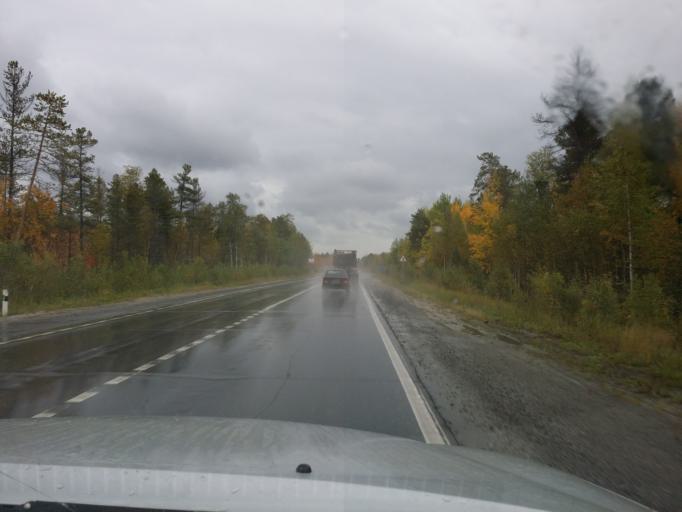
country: RU
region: Khanty-Mansiyskiy Avtonomnyy Okrug
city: Megion
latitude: 61.1310
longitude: 75.7764
